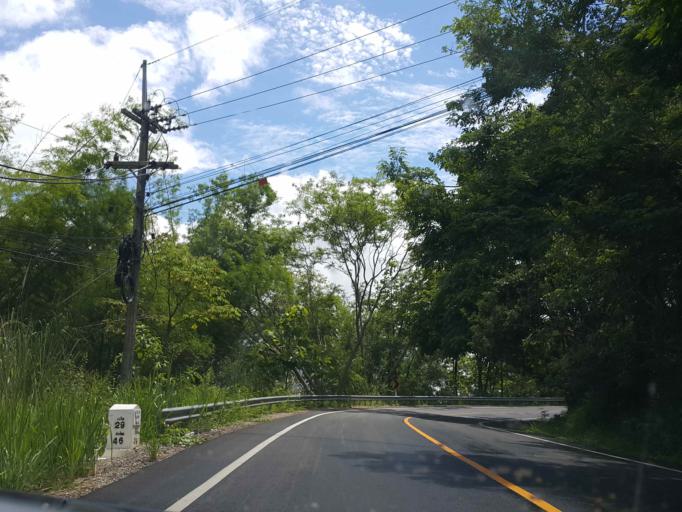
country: TH
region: Chiang Mai
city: Samoeng
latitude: 18.8471
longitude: 98.7731
